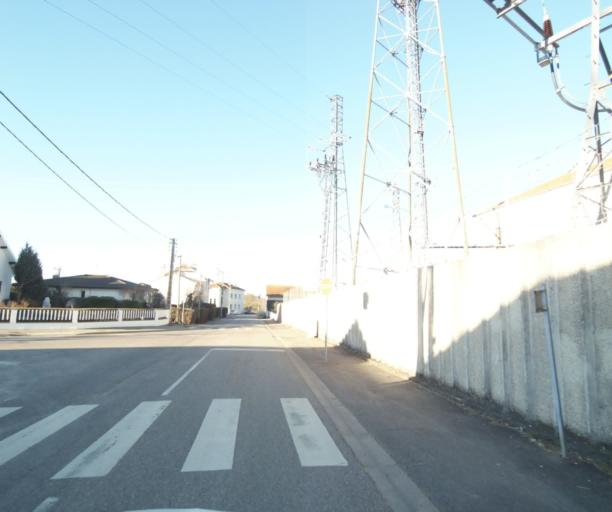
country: FR
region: Lorraine
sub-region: Departement de Meurthe-et-Moselle
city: Laneuveville-devant-Nancy
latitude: 48.6491
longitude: 6.2332
